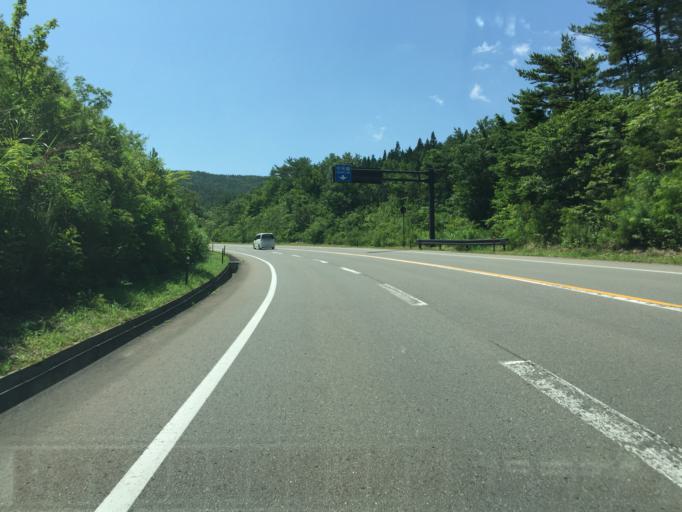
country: JP
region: Fukushima
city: Nihommatsu
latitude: 37.6705
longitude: 140.3372
